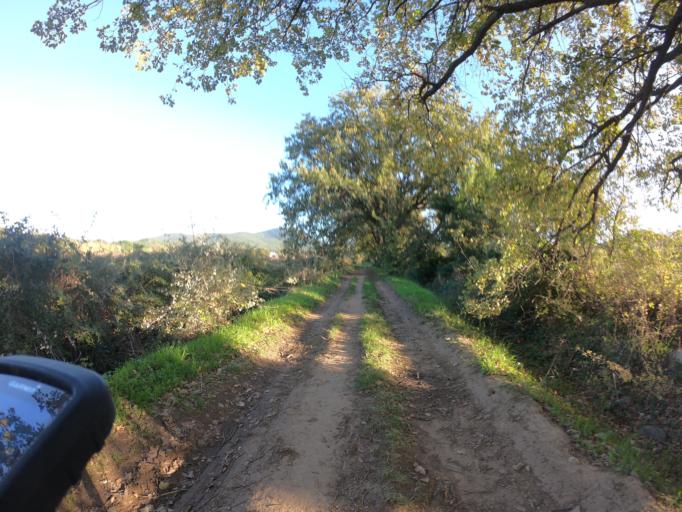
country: FR
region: Provence-Alpes-Cote d'Azur
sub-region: Departement du Var
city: Le Pradet
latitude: 43.1119
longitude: 6.0411
